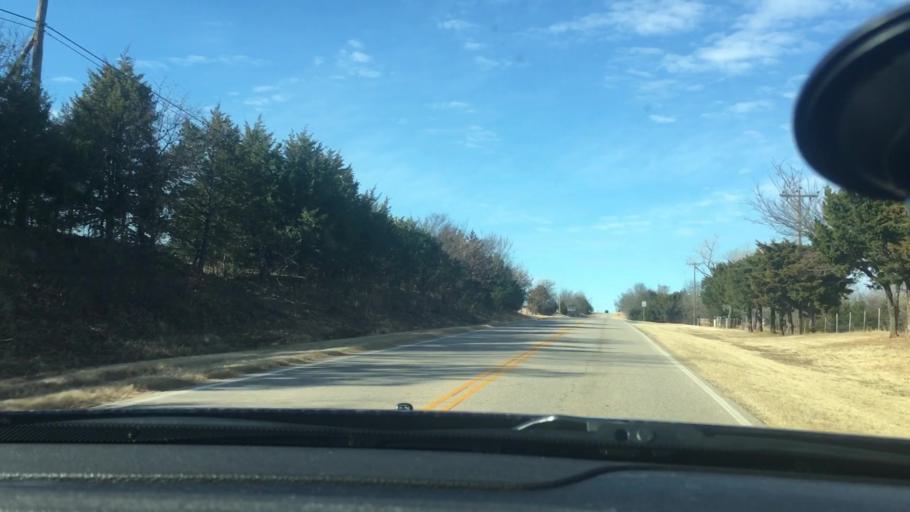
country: US
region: Oklahoma
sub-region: Seminole County
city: Konawa
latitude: 34.9860
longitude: -96.9340
